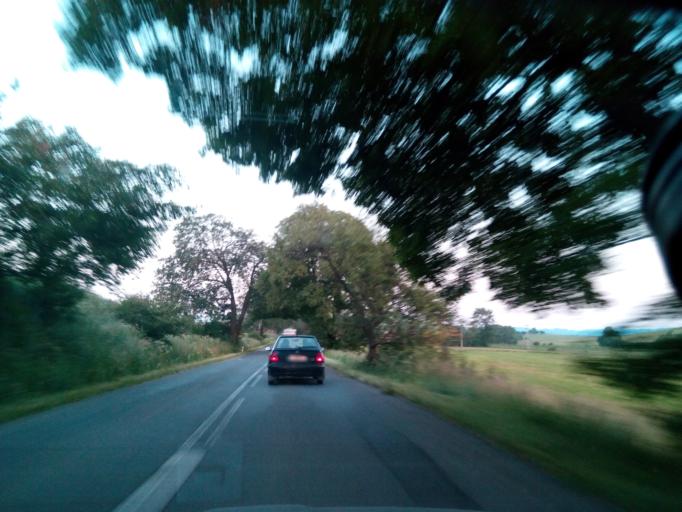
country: SK
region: Presovsky
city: Lubica
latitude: 49.0488
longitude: 20.4363
